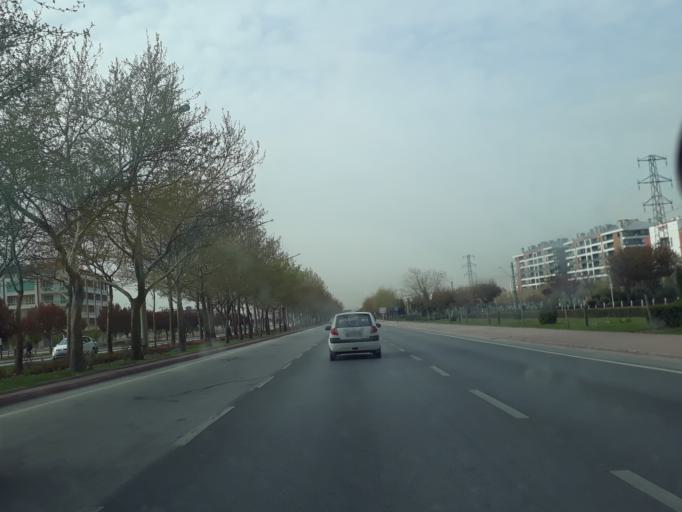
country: TR
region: Konya
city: Selcuklu
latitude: 37.9735
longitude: 32.5160
